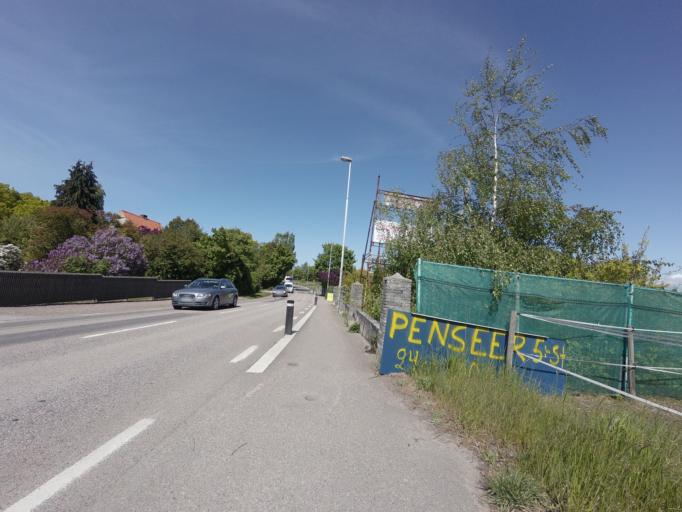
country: SE
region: Skane
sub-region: Helsingborg
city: Odakra
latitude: 56.1265
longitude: 12.6943
